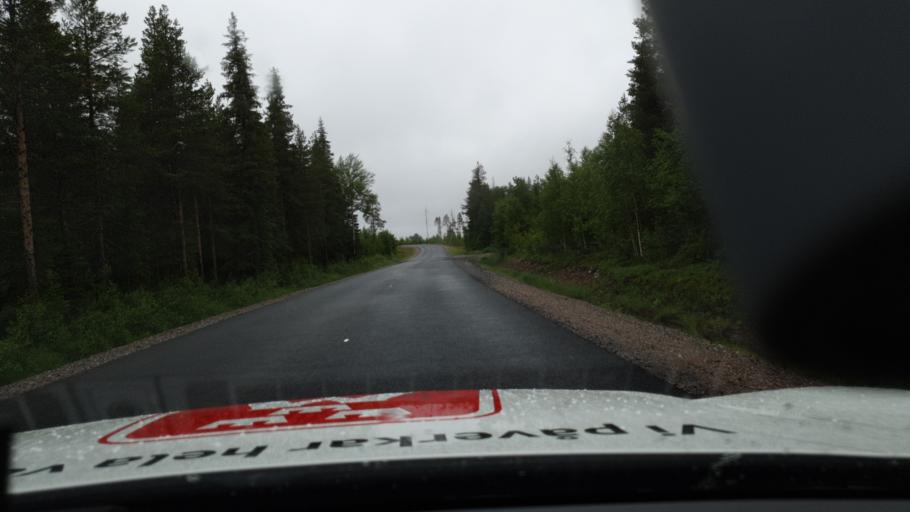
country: SE
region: Norrbotten
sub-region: Overtornea Kommun
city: OEvertornea
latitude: 66.5577
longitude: 23.3370
